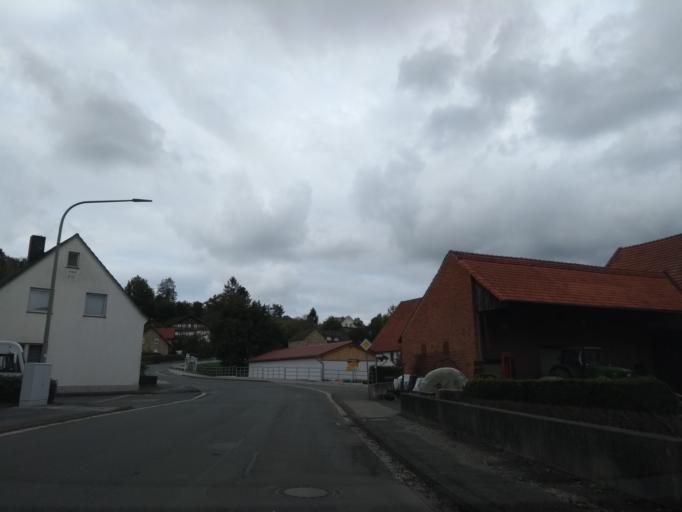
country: DE
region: North Rhine-Westphalia
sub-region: Regierungsbezirk Detmold
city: Paderborn
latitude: 51.6312
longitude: 8.7606
